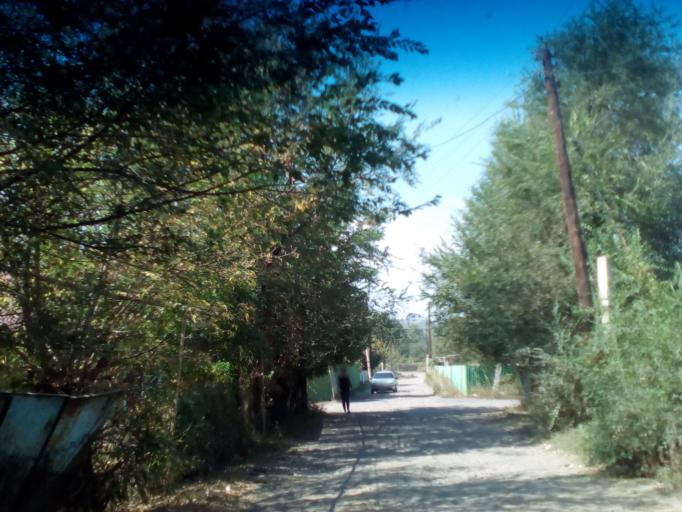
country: KZ
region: Almaty Oblysy
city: Burunday
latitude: 43.1599
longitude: 76.4042
